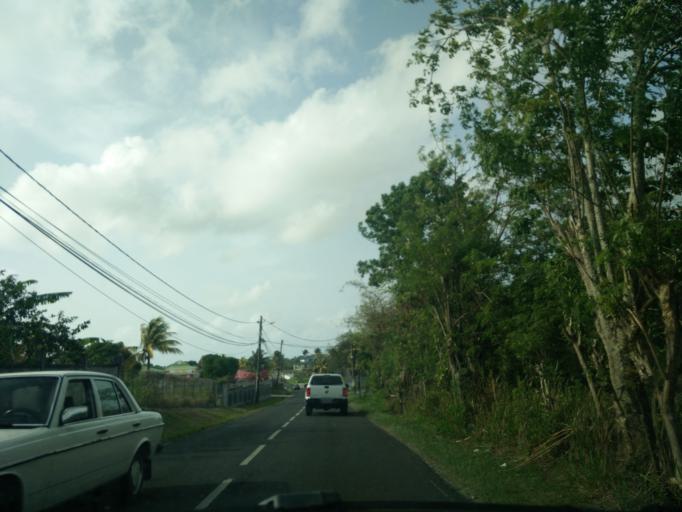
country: GP
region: Guadeloupe
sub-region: Guadeloupe
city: Sainte-Anne
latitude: 16.2727
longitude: -61.3749
